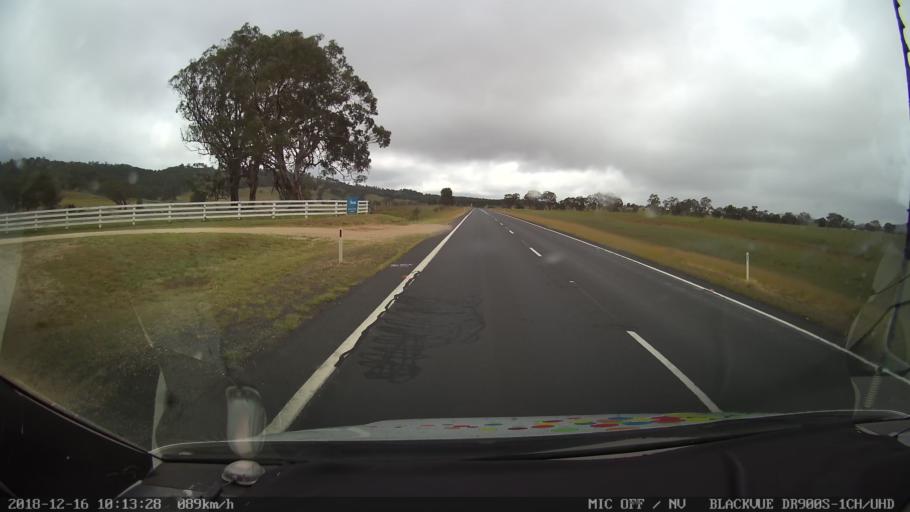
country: AU
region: New South Wales
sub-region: Glen Innes Severn
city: Glen Innes
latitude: -29.2970
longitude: 151.9529
